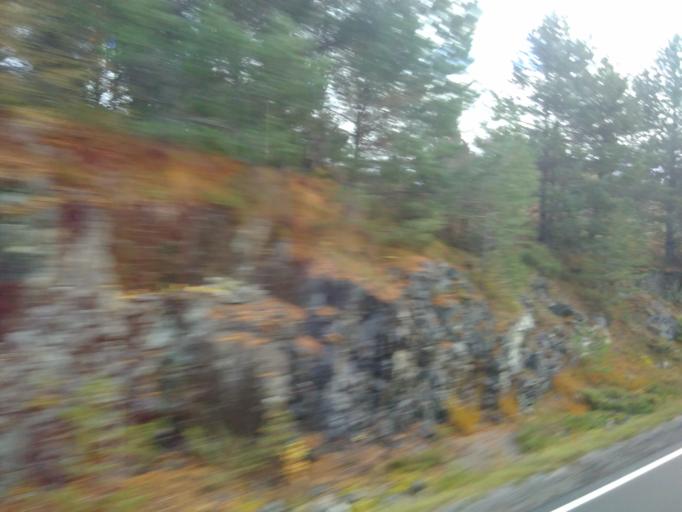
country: NO
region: Sor-Trondelag
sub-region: Hitra
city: Fillan
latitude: 63.5240
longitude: 9.0790
